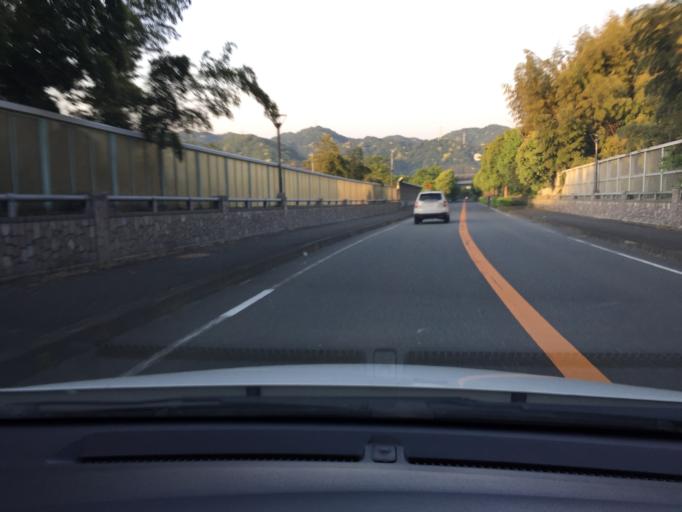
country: JP
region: Kanagawa
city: Hayama
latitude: 35.2621
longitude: 139.6059
